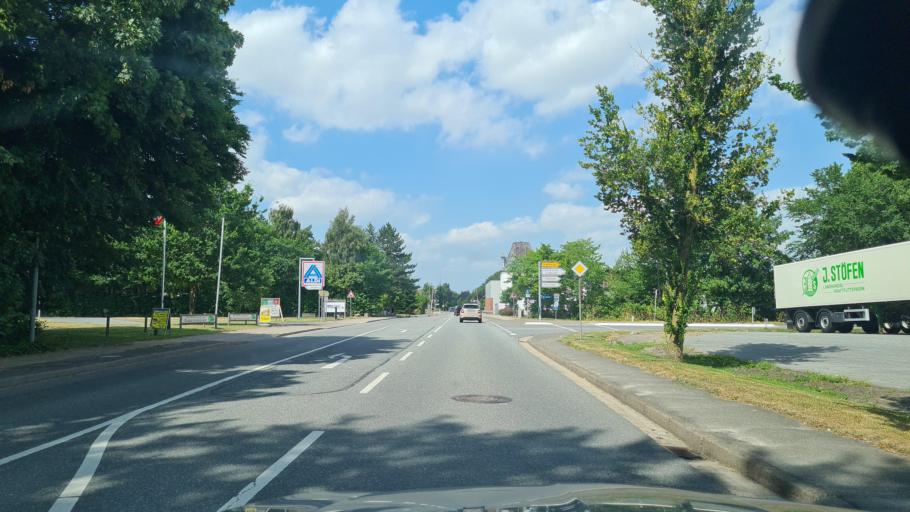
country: DE
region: Schleswig-Holstein
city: Wesselburen
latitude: 54.2053
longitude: 8.9335
